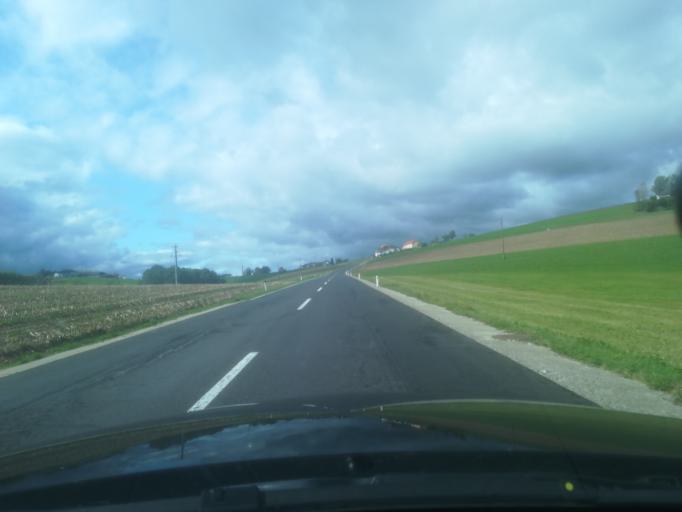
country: AT
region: Upper Austria
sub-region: Politischer Bezirk Urfahr-Umgebung
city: Gramastetten
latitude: 48.3907
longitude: 14.1877
